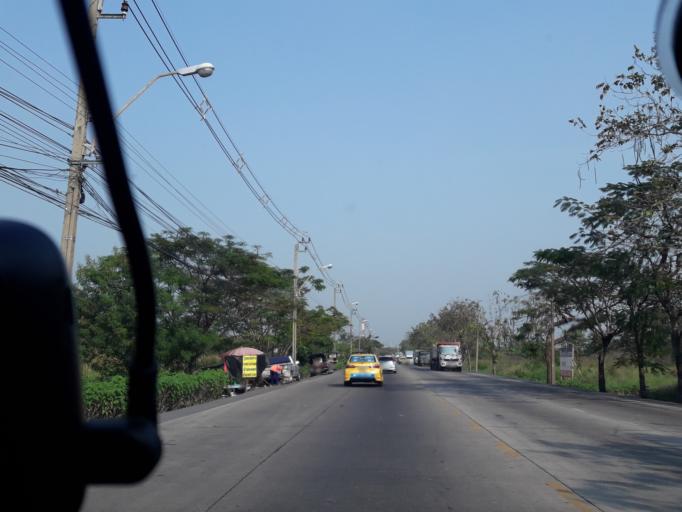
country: TH
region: Bangkok
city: Khlong Sam Wa
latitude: 13.8591
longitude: 100.7242
